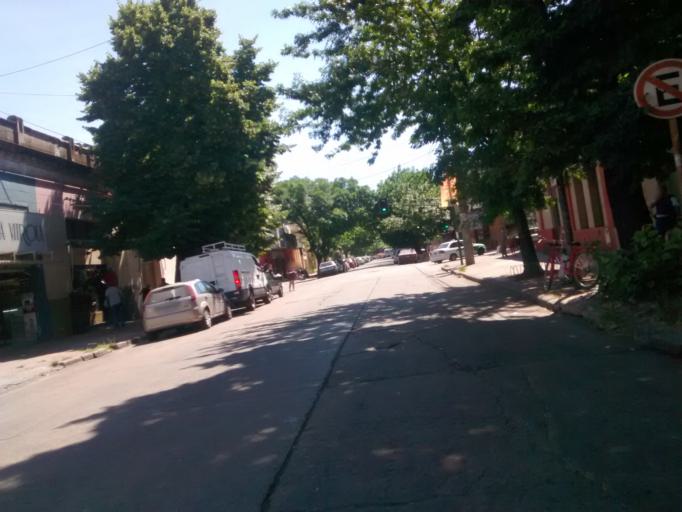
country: AR
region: Buenos Aires
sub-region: Partido de La Plata
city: La Plata
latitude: -34.9056
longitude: -57.9538
